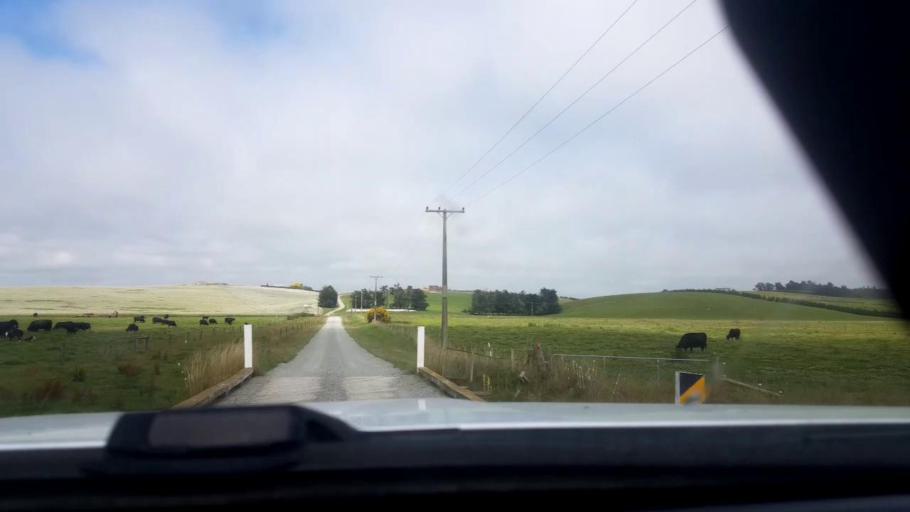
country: NZ
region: Canterbury
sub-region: Timaru District
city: Timaru
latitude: -44.3289
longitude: 171.2038
